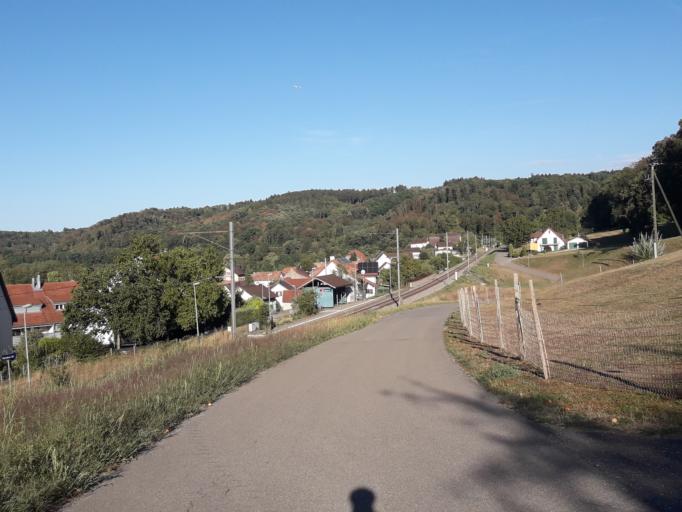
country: DE
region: Baden-Wuerttemberg
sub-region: Freiburg Region
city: Hohentengen am Hochrhein
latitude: 47.5654
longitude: 8.3728
